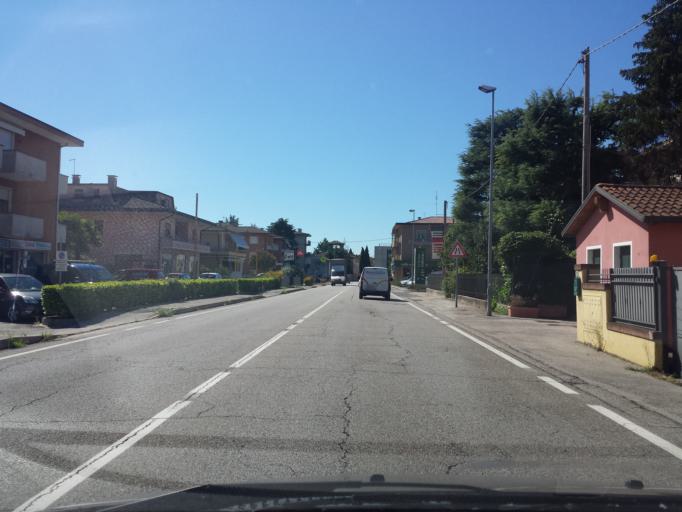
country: IT
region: Veneto
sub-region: Provincia di Vicenza
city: Dueville
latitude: 45.6299
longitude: 11.5708
